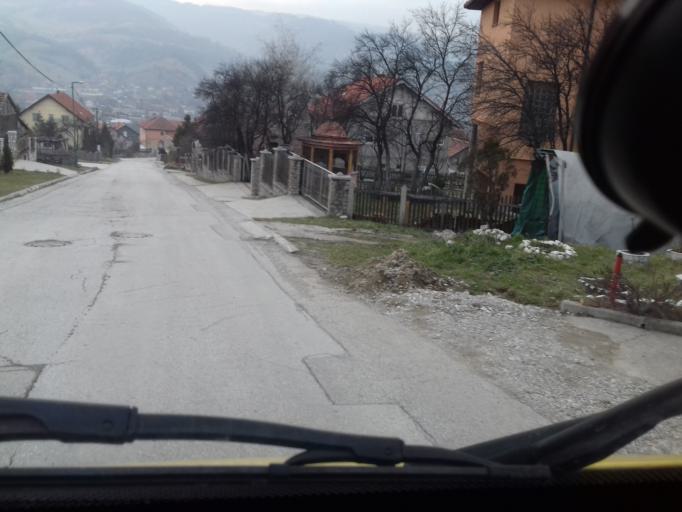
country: BA
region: Federation of Bosnia and Herzegovina
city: Kakanj
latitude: 44.1288
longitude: 18.1104
